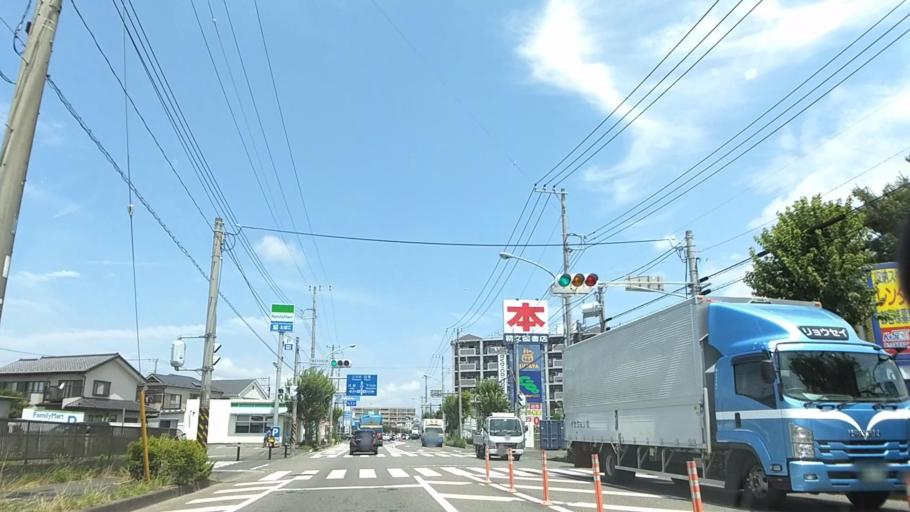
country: JP
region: Kanagawa
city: Minami-rinkan
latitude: 35.4573
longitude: 139.4811
